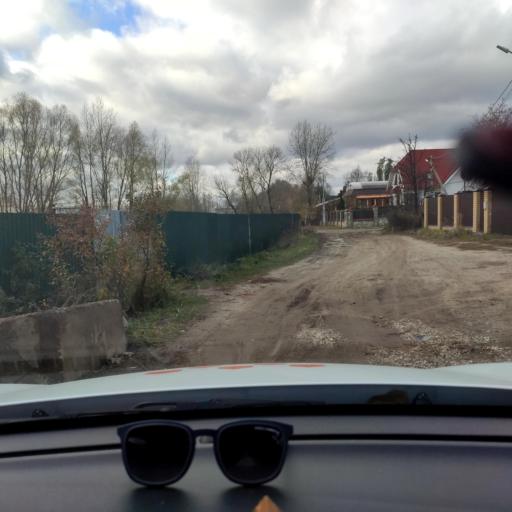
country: RU
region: Tatarstan
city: Verkhniy Uslon
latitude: 55.7990
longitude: 49.0288
